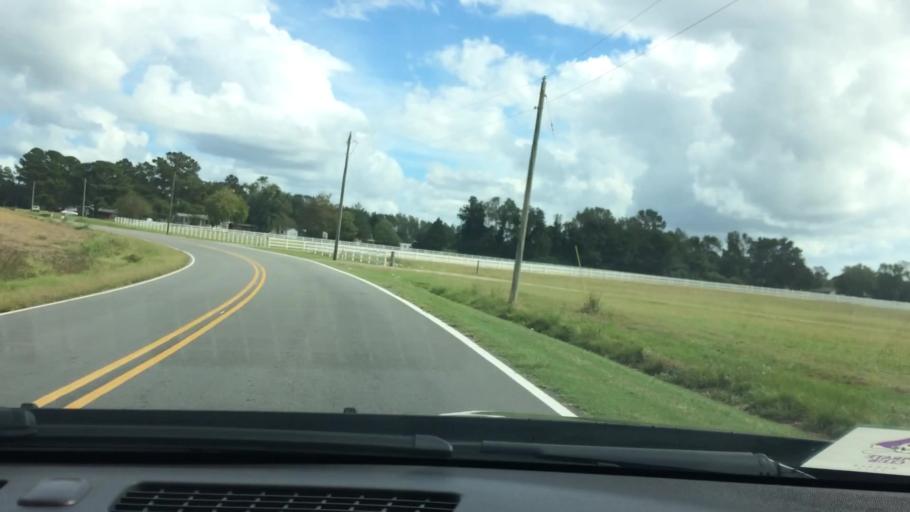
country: US
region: North Carolina
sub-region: Pitt County
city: Ayden
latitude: 35.4556
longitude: -77.4814
